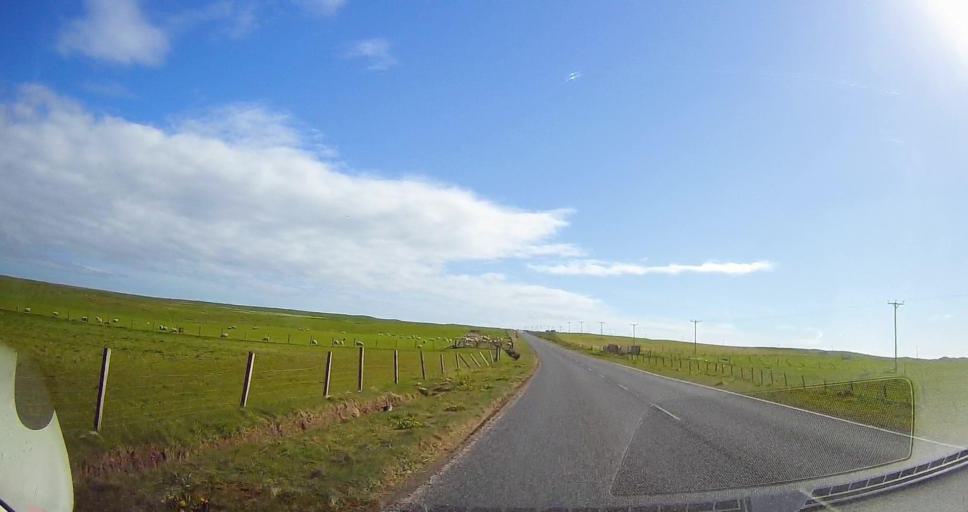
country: GB
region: Scotland
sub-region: Shetland Islands
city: Sandwick
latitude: 59.9076
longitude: -1.3016
